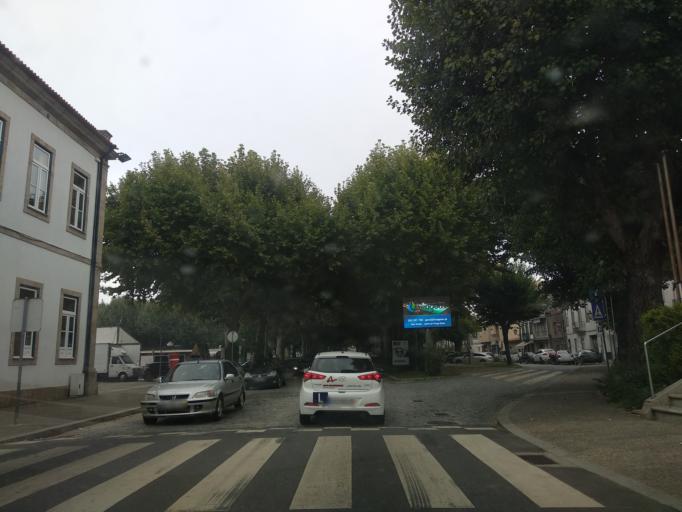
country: PT
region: Braga
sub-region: Vila Verde
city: Vila Verde
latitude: 41.6491
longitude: -8.4359
